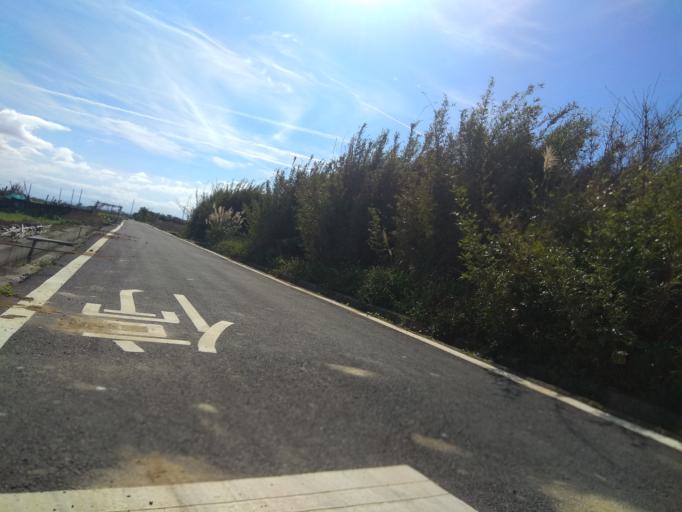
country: TW
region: Taiwan
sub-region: Hsinchu
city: Zhubei
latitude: 24.9985
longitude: 121.0386
